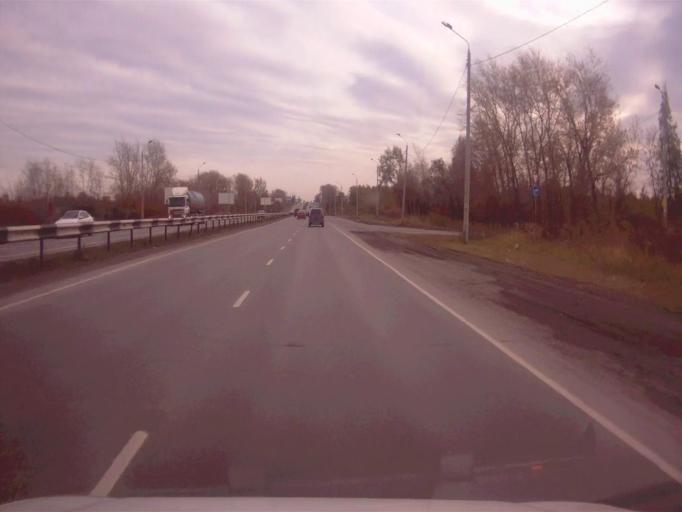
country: RU
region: Chelyabinsk
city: Novosineglazovskiy
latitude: 55.0608
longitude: 61.4015
